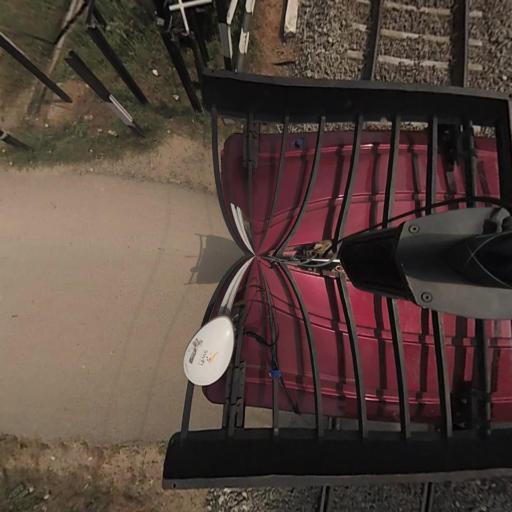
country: IN
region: Telangana
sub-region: Nalgonda
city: Nalgonda
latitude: 17.2134
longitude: 79.1600
